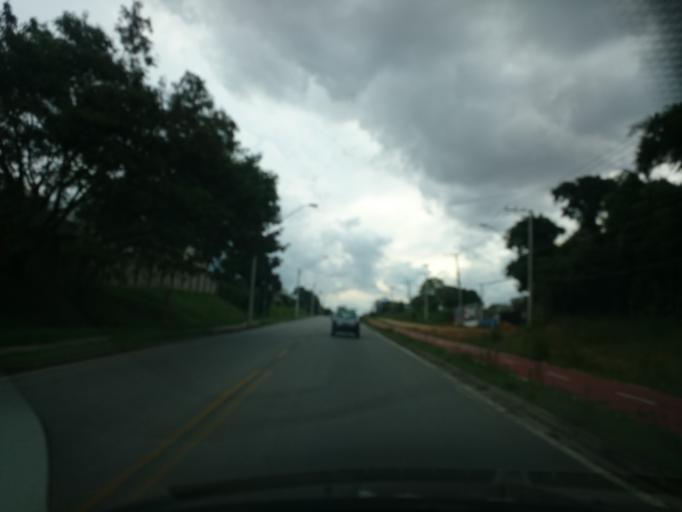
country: BR
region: Sao Paulo
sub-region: Sorocaba
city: Sorocaba
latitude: -23.4772
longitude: -47.4130
